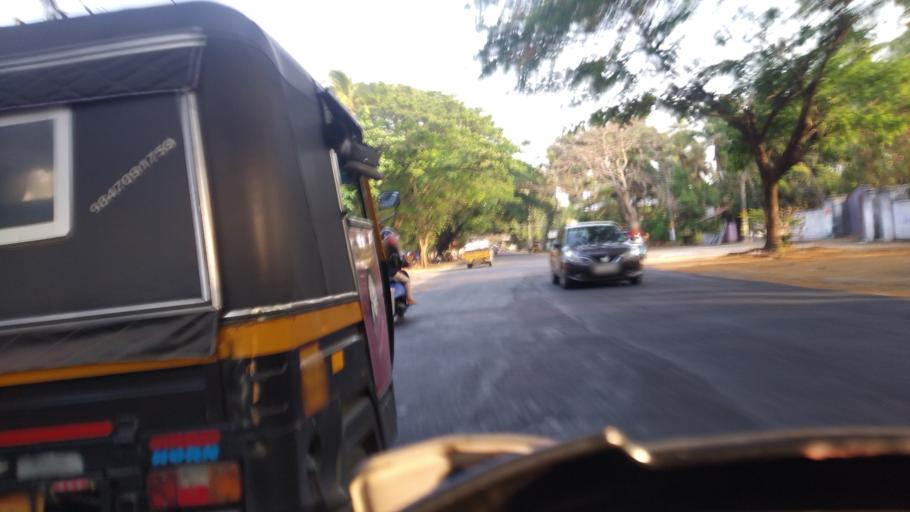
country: IN
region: Kerala
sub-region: Thrissur District
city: Thanniyam
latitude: 10.4317
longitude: 76.0993
